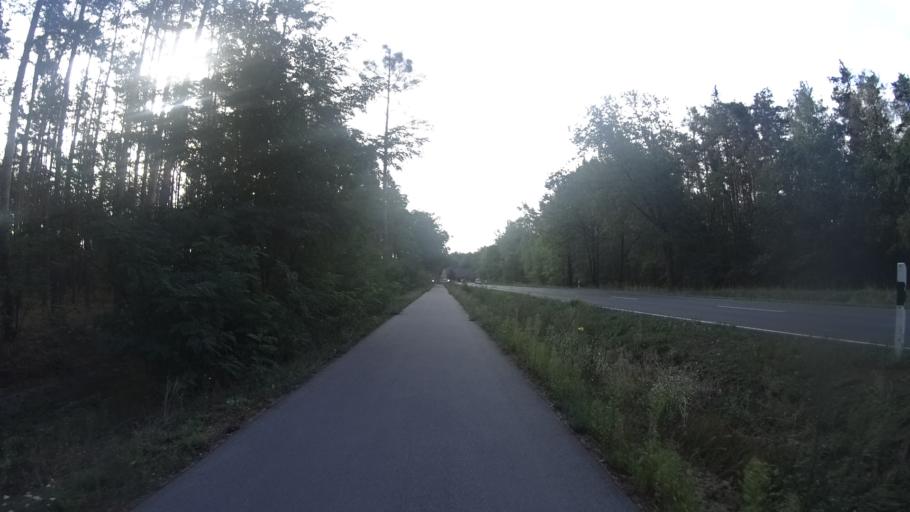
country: DE
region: Brandenburg
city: Premnitz
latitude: 52.5184
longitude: 12.3994
